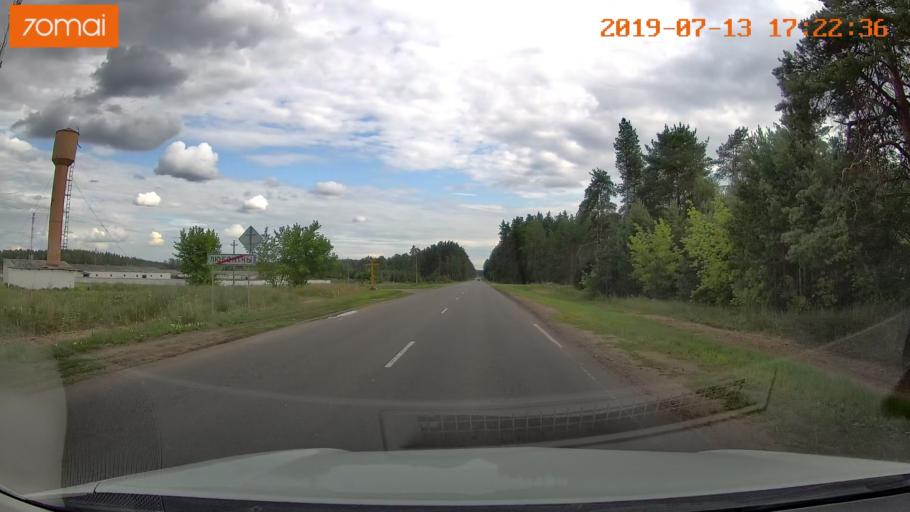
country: BY
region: Mogilev
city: Babruysk
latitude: 53.2695
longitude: 29.2347
